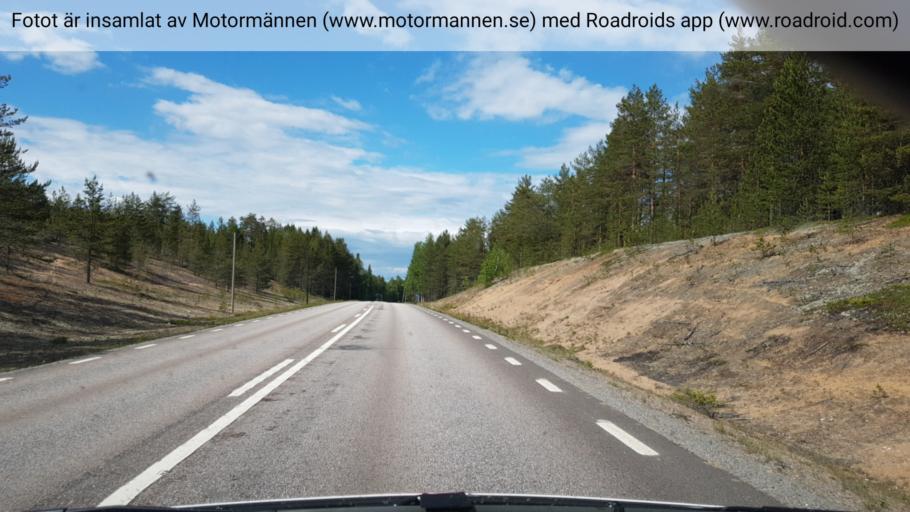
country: SE
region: Norrbotten
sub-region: Overkalix Kommun
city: OEverkalix
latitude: 66.2849
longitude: 22.8187
